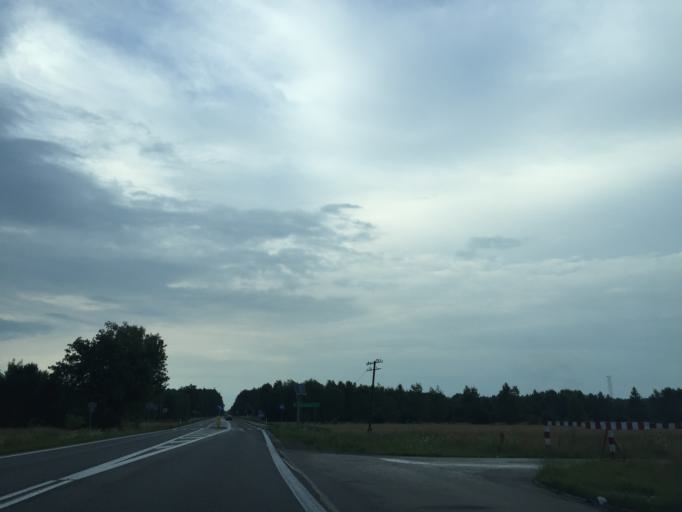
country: PL
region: Masovian Voivodeship
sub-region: Powiat ostrowski
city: Brok
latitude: 52.7493
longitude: 21.8551
